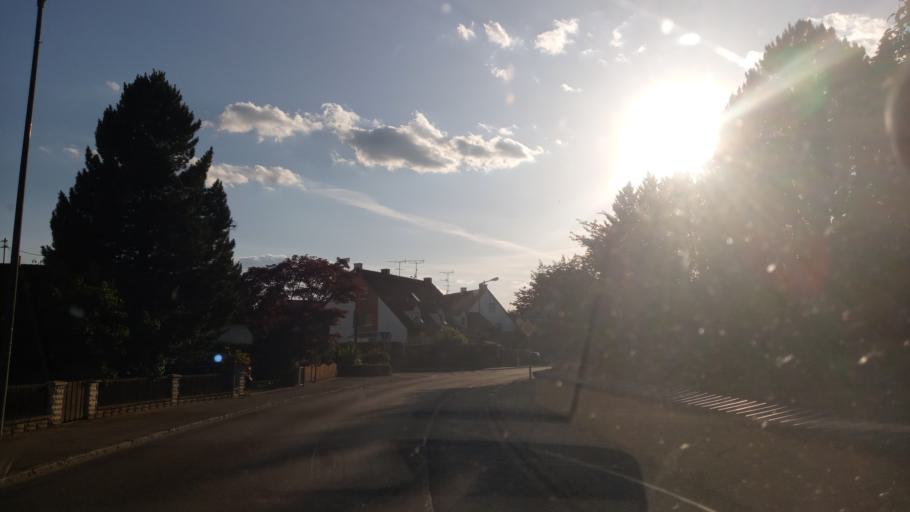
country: DE
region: Bavaria
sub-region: Upper Bavaria
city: Weichs
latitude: 48.3812
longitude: 11.4190
